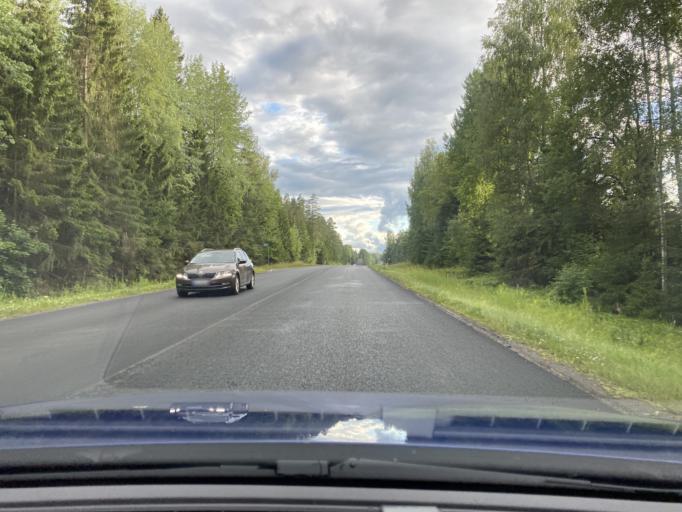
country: FI
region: Haeme
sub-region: Haemeenlinna
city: Haemeenlinna
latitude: 60.9498
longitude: 24.4026
